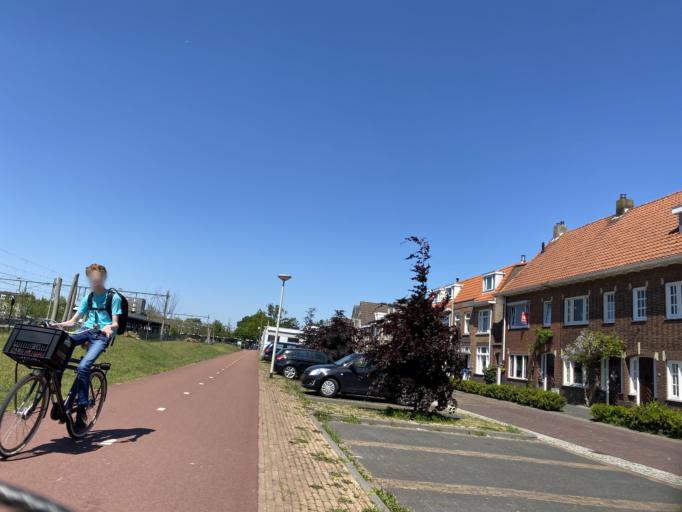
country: NL
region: North Brabant
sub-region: Gemeente Bergen op Zoom
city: Bergen op Zoom
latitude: 51.4930
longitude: 4.2963
